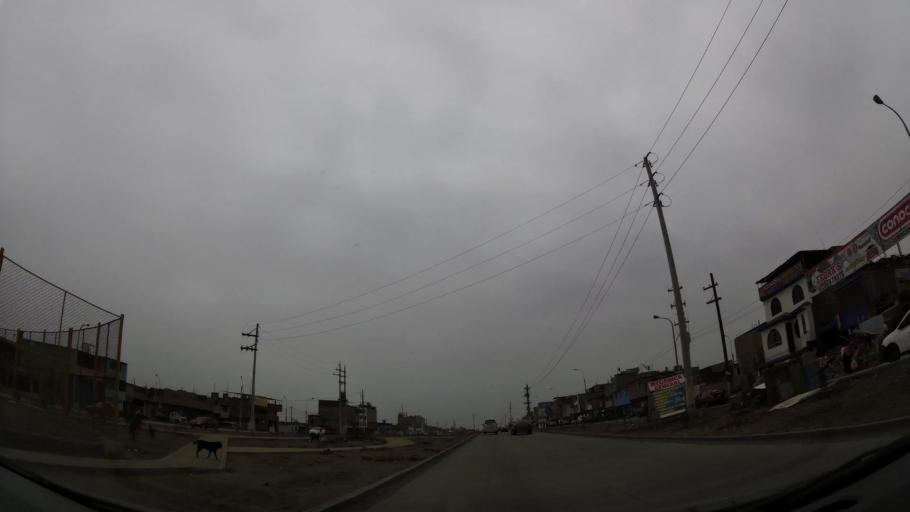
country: PE
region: Lima
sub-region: Lima
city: Surco
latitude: -12.2123
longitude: -76.9490
